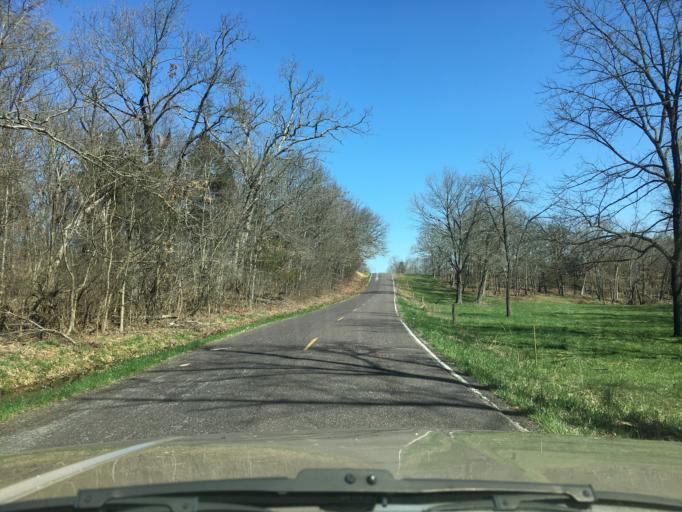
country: US
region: Missouri
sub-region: Franklin County
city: New Haven
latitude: 38.5427
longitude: -91.3303
